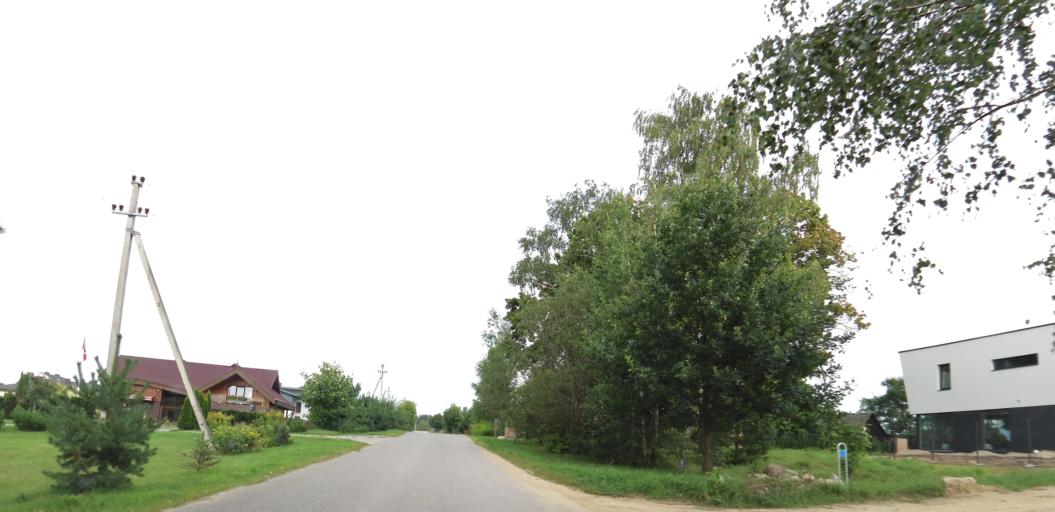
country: LT
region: Vilnius County
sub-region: Vilnius
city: Fabijoniskes
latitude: 54.7521
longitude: 25.2349
